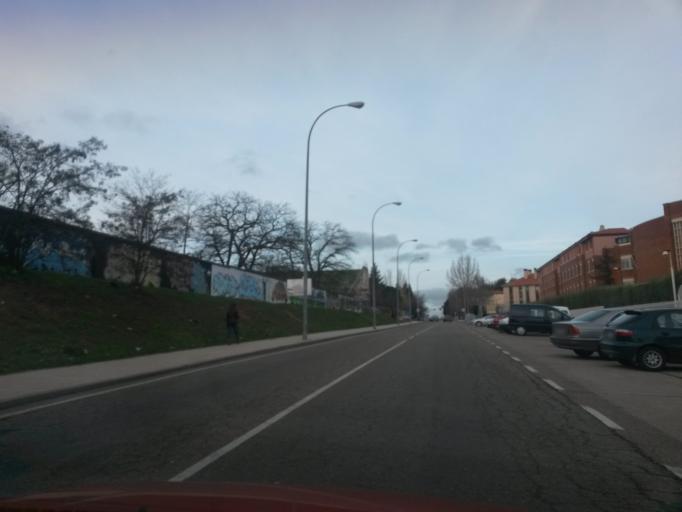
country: ES
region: Castille and Leon
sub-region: Provincia de Salamanca
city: Salamanca
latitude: 40.9800
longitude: -5.6613
